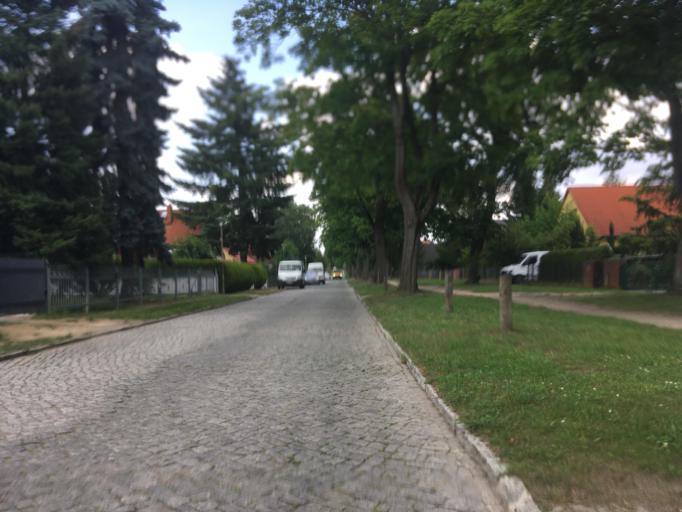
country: DE
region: Brandenburg
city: Wildau
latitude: 52.3340
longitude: 13.6235
